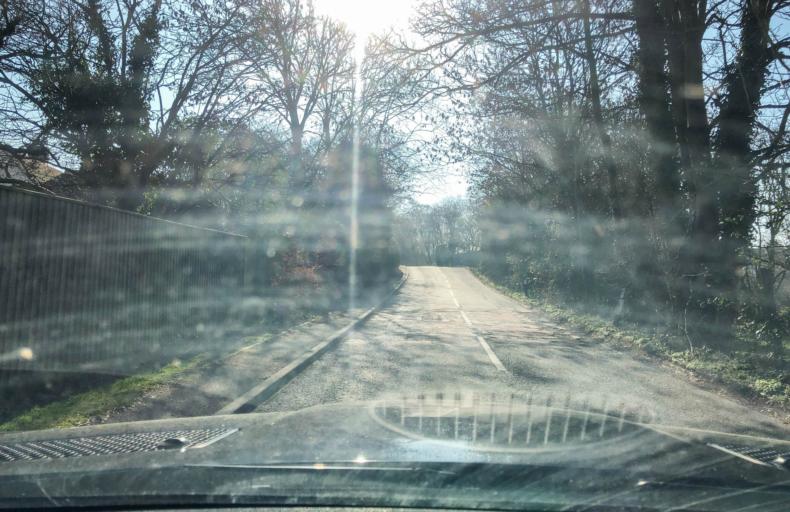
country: GB
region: England
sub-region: Warwickshire
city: Wellesbourne Mountford
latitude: 52.1606
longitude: -1.5114
